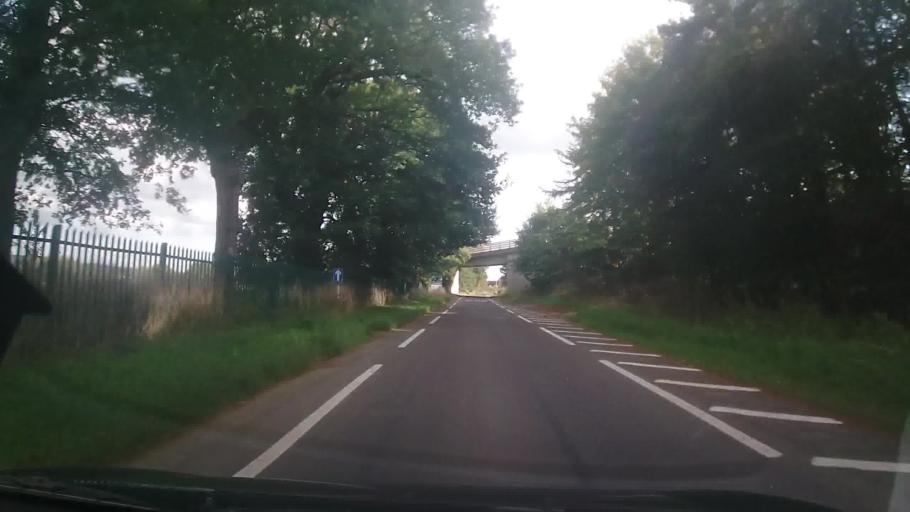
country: GB
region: England
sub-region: Shropshire
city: Ludlow
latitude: 52.3820
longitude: -2.7310
